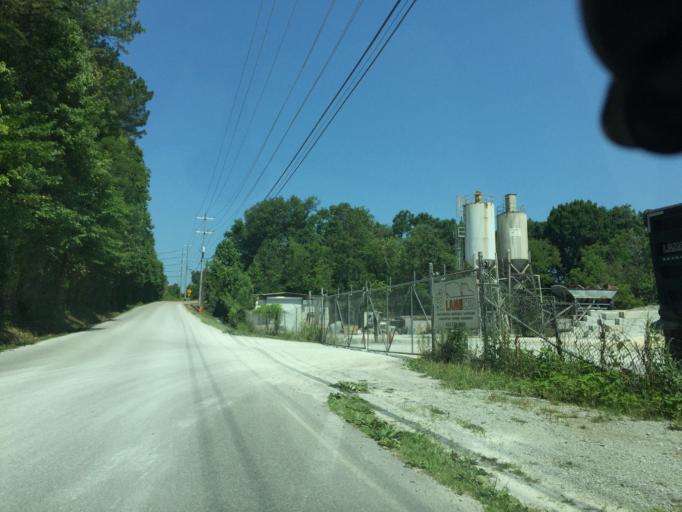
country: US
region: Tennessee
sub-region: Hamilton County
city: Collegedale
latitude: 35.0784
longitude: -85.0671
